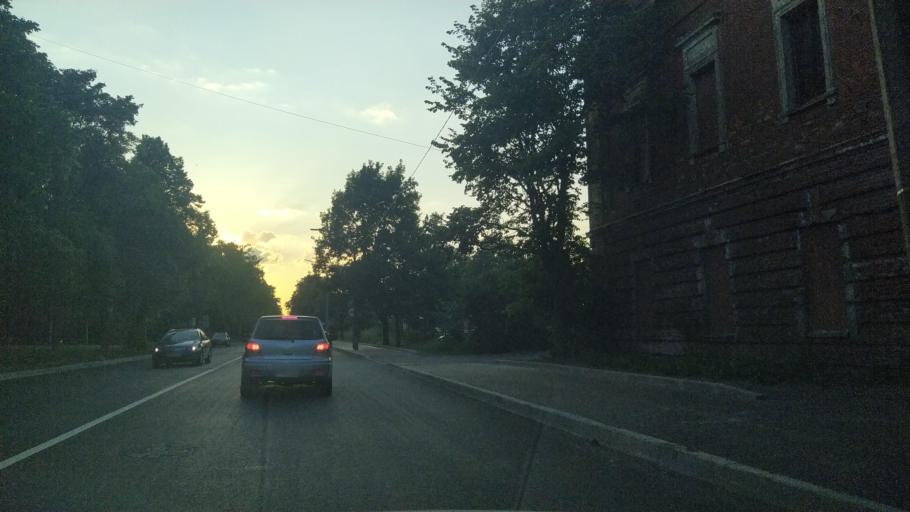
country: RU
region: St.-Petersburg
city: Kronshtadt
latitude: 59.9974
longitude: 29.7765
